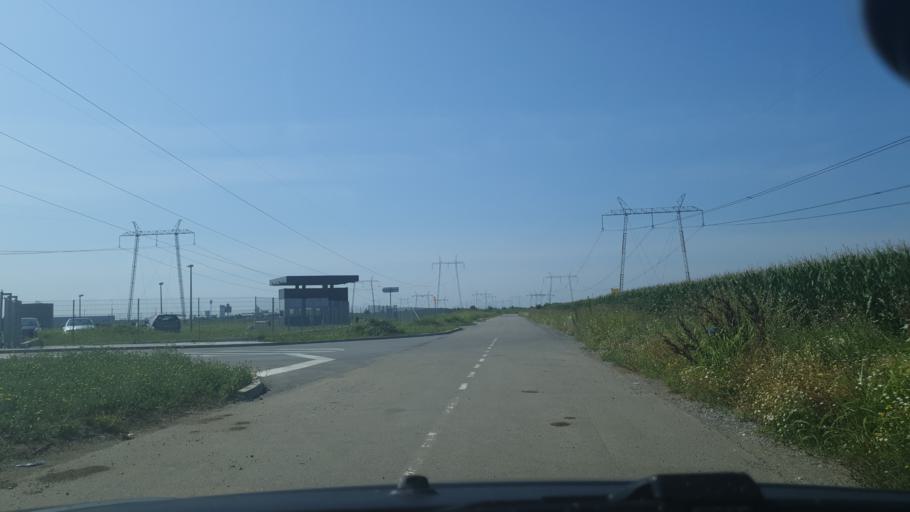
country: RS
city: Simanovci
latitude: 44.8936
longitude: 20.1060
